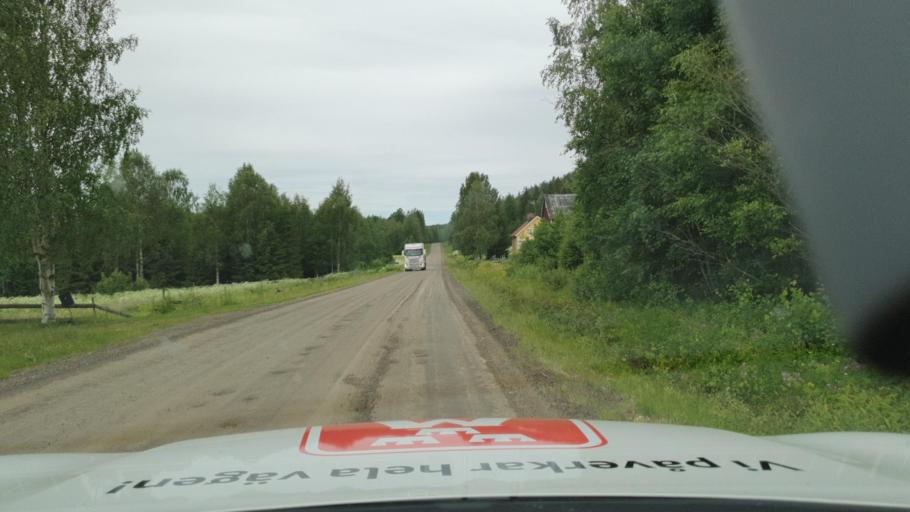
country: SE
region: Vaesterbotten
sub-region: Skelleftea Kommun
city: Burtraesk
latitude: 64.3330
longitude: 20.6164
